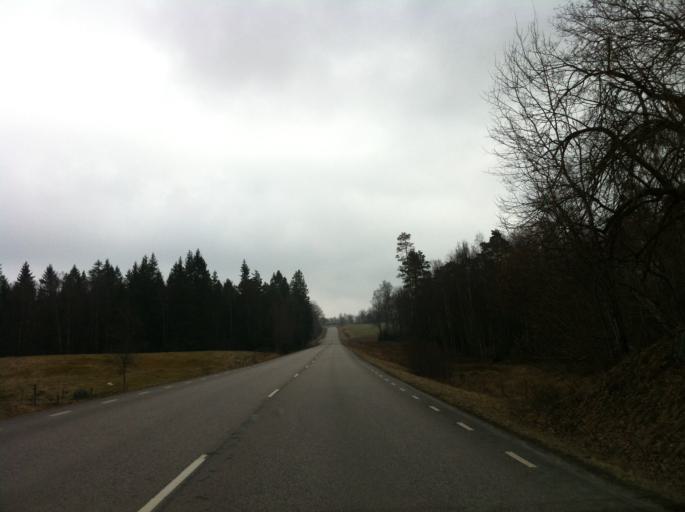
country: SE
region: Vaestra Goetaland
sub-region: Boras Kommun
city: Dalsjofors
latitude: 57.7737
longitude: 13.1028
